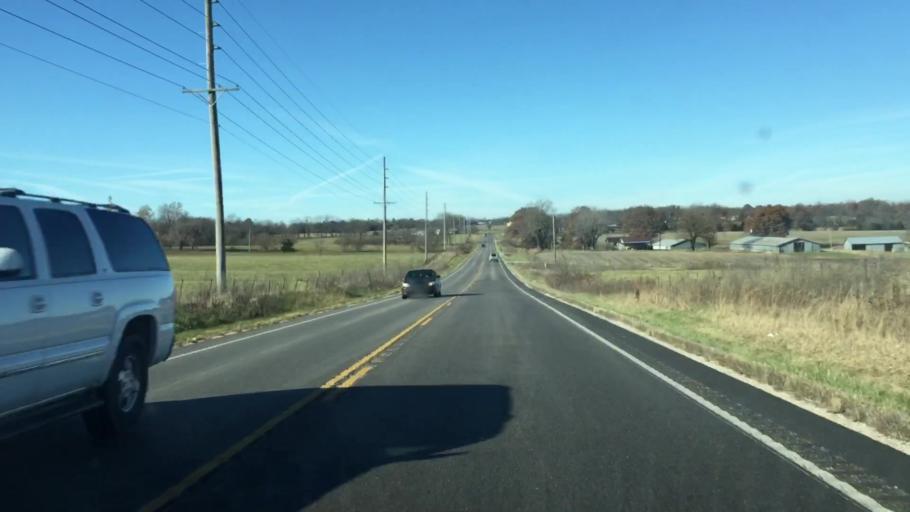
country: US
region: Missouri
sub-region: Miller County
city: Eldon
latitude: 38.3738
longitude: -92.6469
